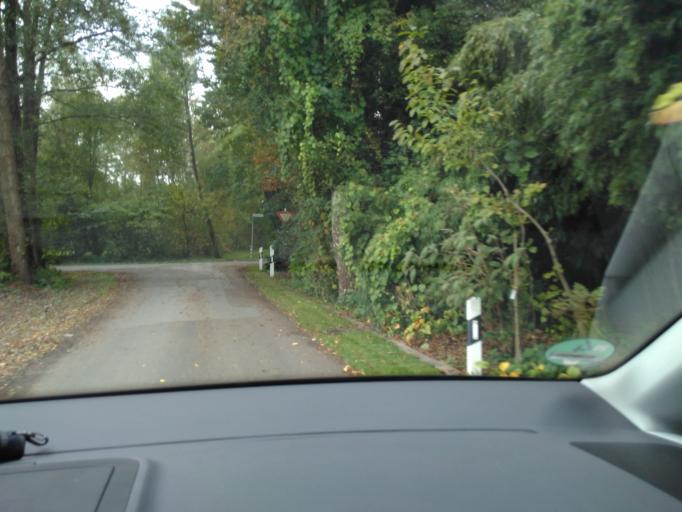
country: DE
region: North Rhine-Westphalia
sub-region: Regierungsbezirk Detmold
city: Verl
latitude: 51.8630
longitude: 8.4875
